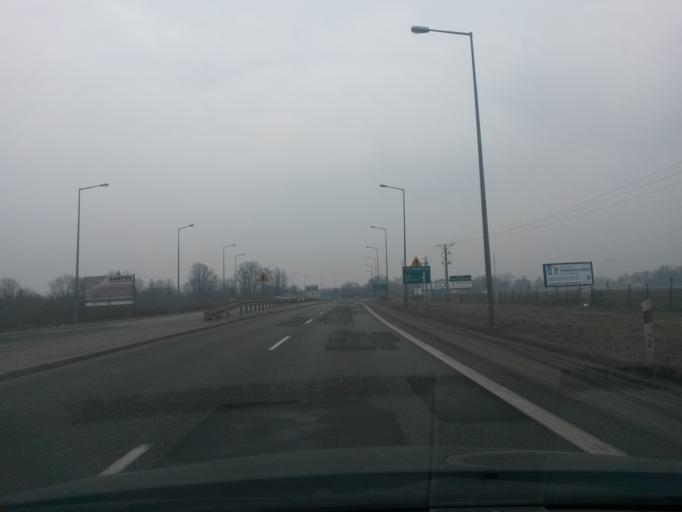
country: PL
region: Masovian Voivodeship
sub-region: Powiat legionowski
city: Bialobrzegi
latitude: 52.4691
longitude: 21.0298
